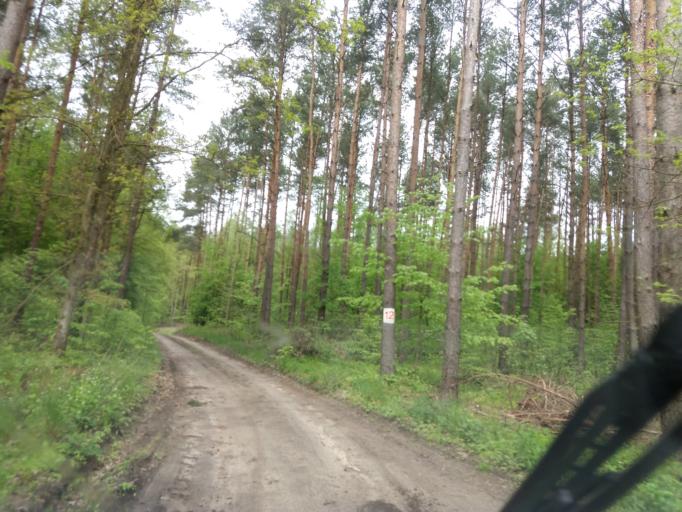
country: PL
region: West Pomeranian Voivodeship
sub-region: Powiat choszczenski
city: Bierzwnik
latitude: 53.0167
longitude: 15.6790
